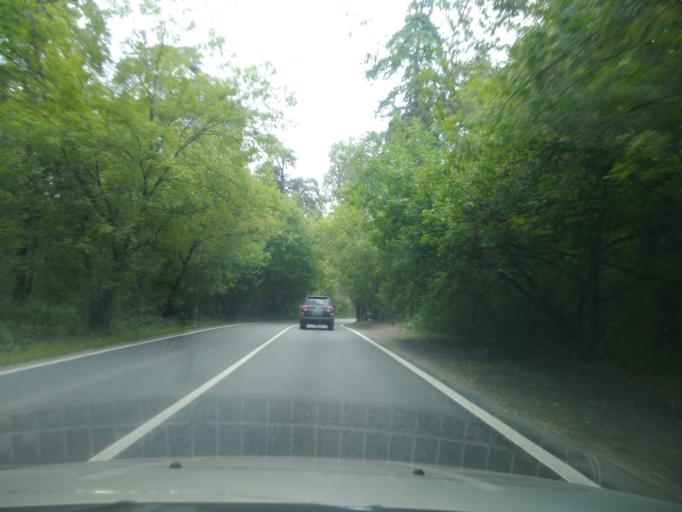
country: RU
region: Moscow
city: Rublevo
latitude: 55.7770
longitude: 37.3566
